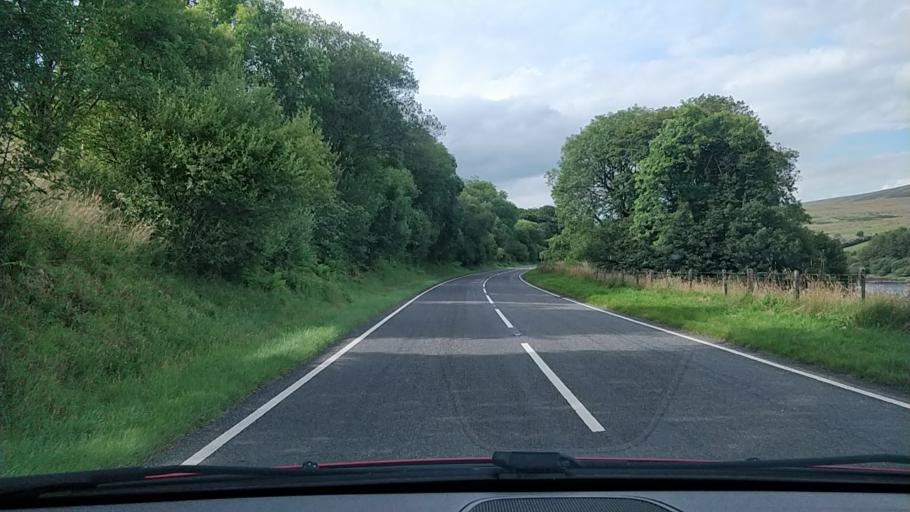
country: GB
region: Wales
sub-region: Gwynedd
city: Bala
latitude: 52.9551
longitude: -3.7206
